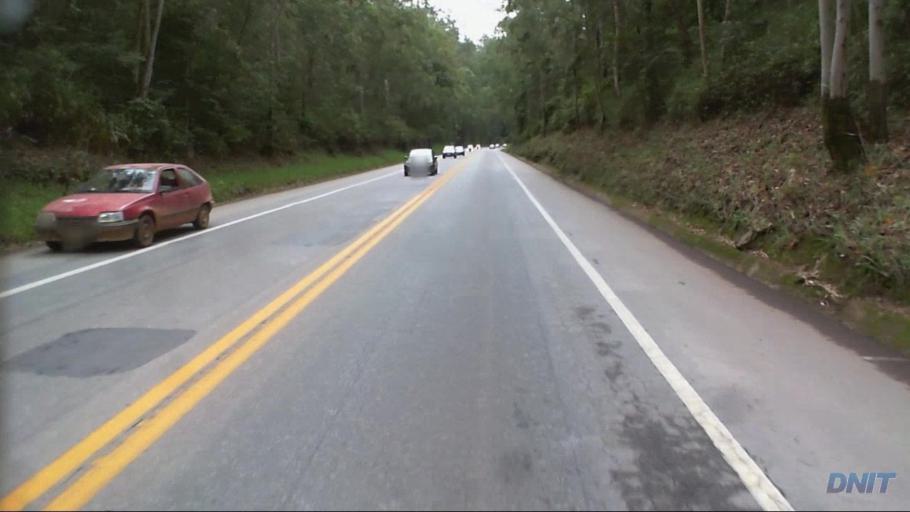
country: BR
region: Minas Gerais
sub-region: Joao Monlevade
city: Joao Monlevade
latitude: -19.8531
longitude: -43.1389
